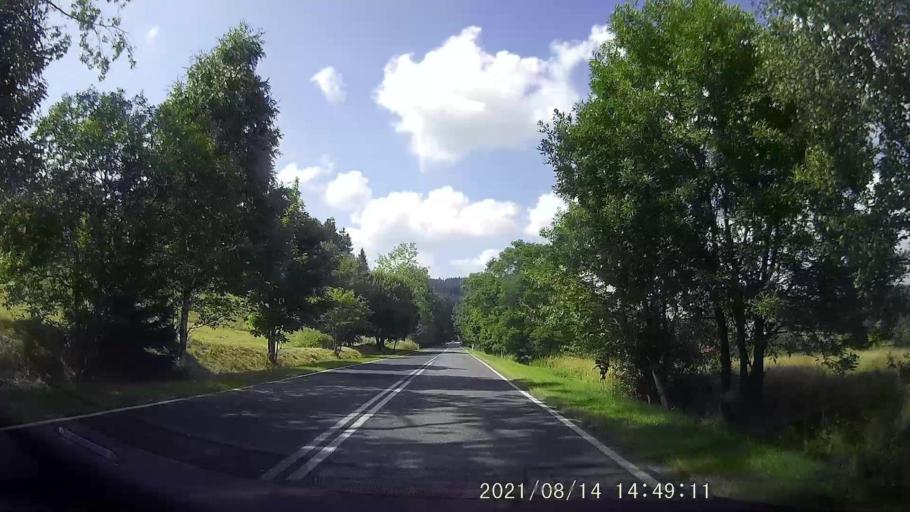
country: PL
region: Lower Silesian Voivodeship
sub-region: Powiat walbrzyski
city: Gluszyca Gorna
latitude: 50.6390
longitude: 16.3885
